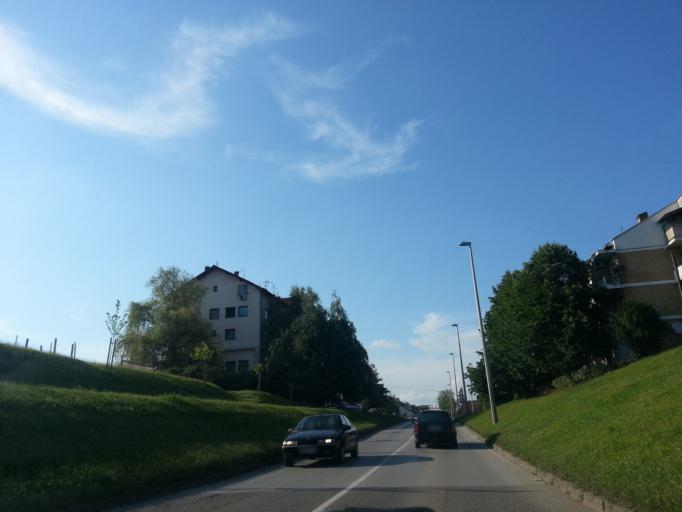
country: BA
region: Brcko
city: Brcko
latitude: 44.8658
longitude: 18.8110
